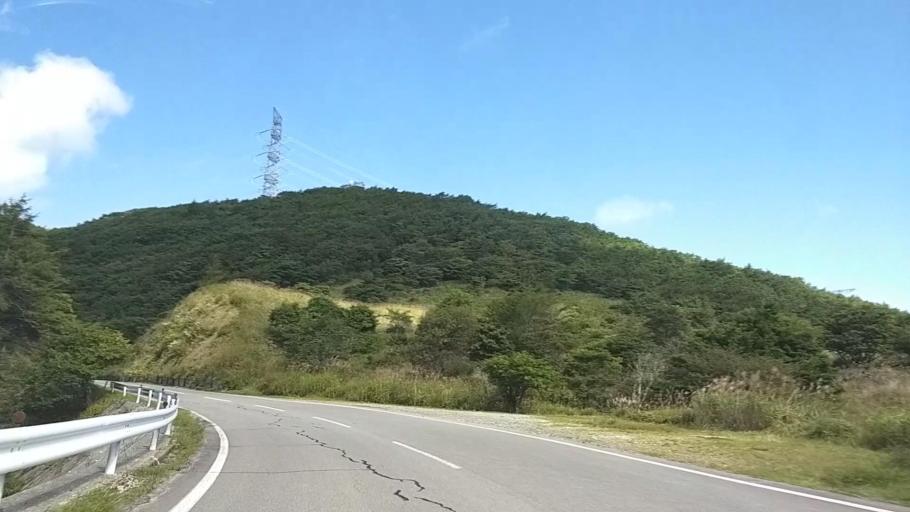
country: JP
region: Nagano
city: Suwa
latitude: 36.1407
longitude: 138.1494
